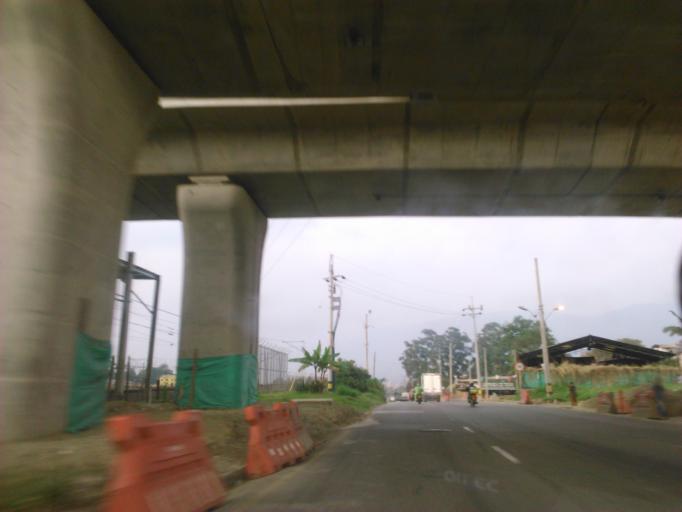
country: CO
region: Antioquia
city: Sabaneta
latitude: 6.1528
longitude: -75.6258
